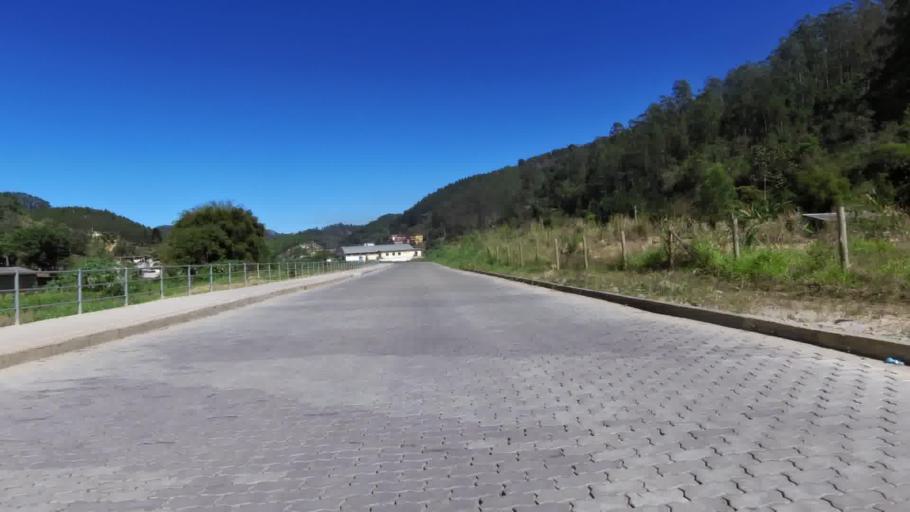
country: BR
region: Espirito Santo
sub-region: Vargem Alta
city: Vargem Alta
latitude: -20.6673
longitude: -41.0003
